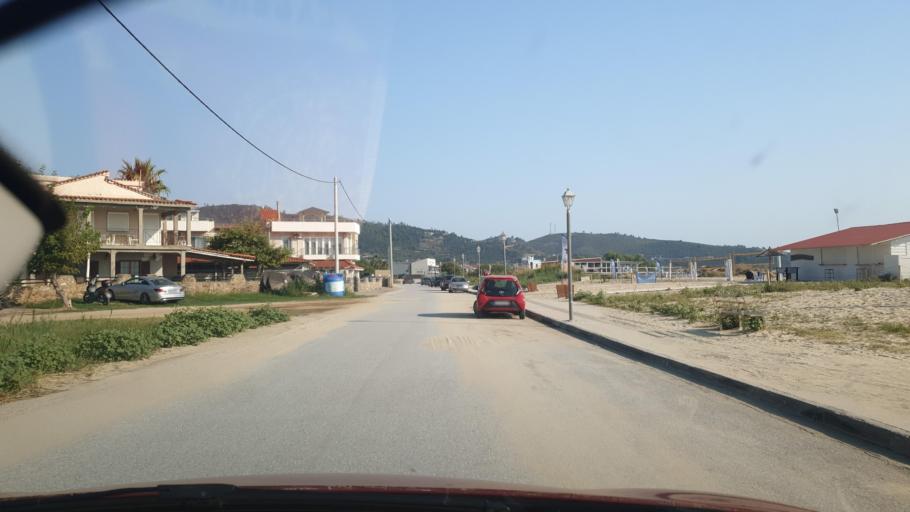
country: GR
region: Central Macedonia
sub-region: Nomos Chalkidikis
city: Sarti
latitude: 40.0838
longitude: 23.9789
